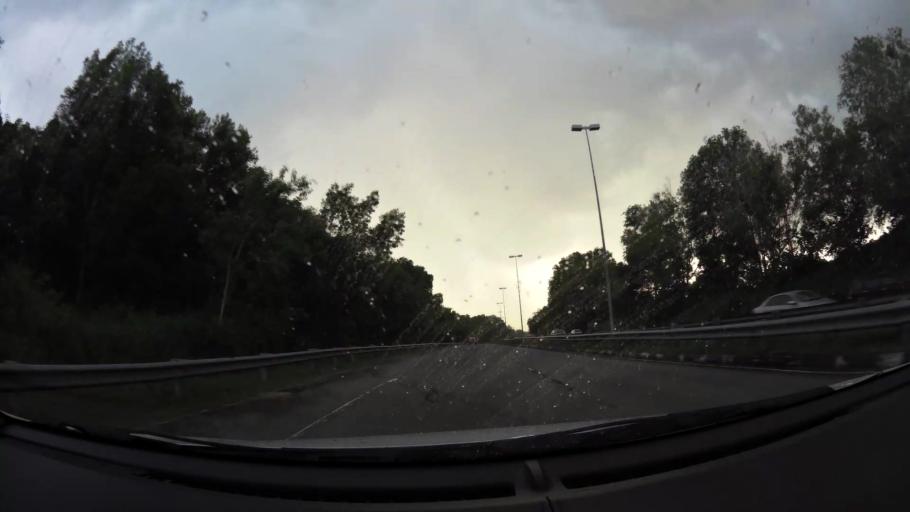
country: BN
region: Brunei and Muara
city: Bandar Seri Begawan
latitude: 4.9278
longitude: 114.9688
